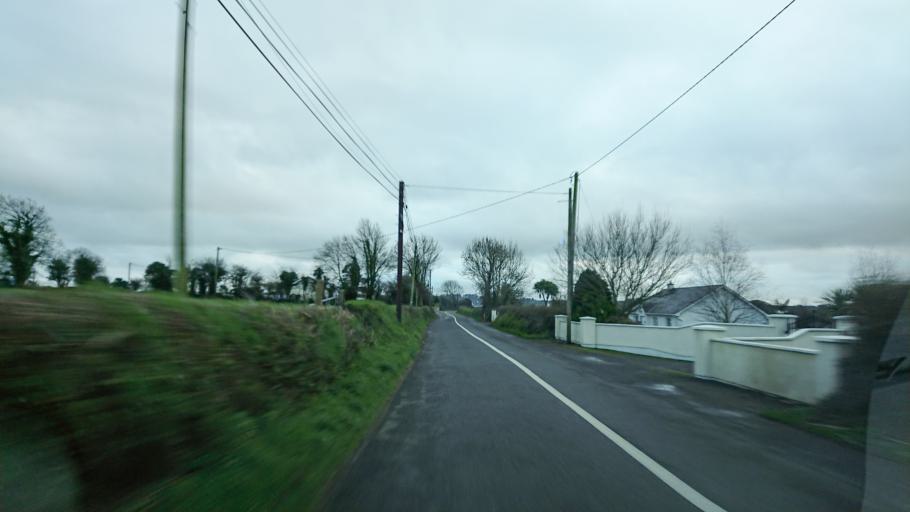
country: IE
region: Munster
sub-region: Waterford
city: Portlaw
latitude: 52.1826
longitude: -7.4085
